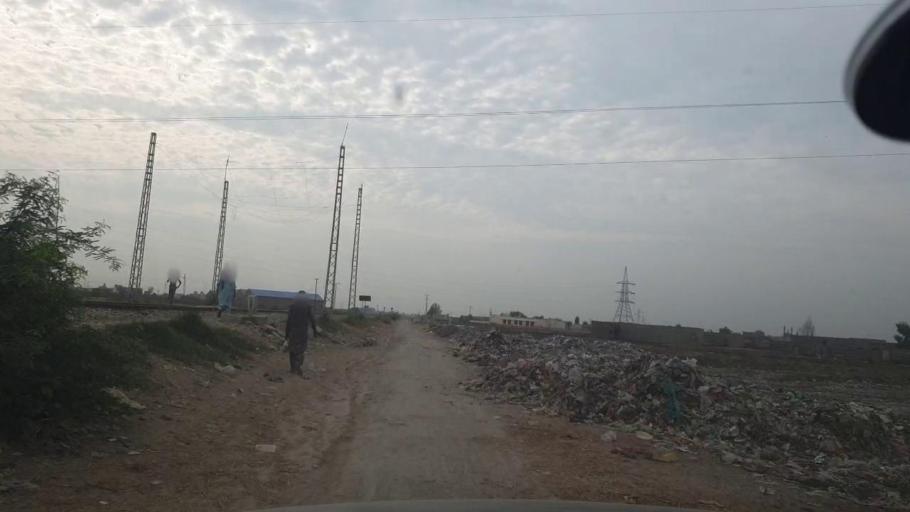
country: PK
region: Sindh
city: Jacobabad
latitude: 28.2615
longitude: 68.4490
